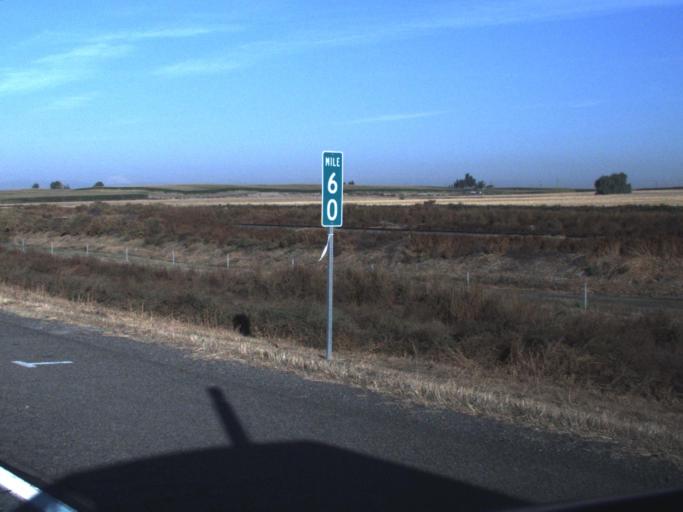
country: US
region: Washington
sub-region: Yakima County
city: Granger
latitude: 46.3385
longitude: -120.1498
